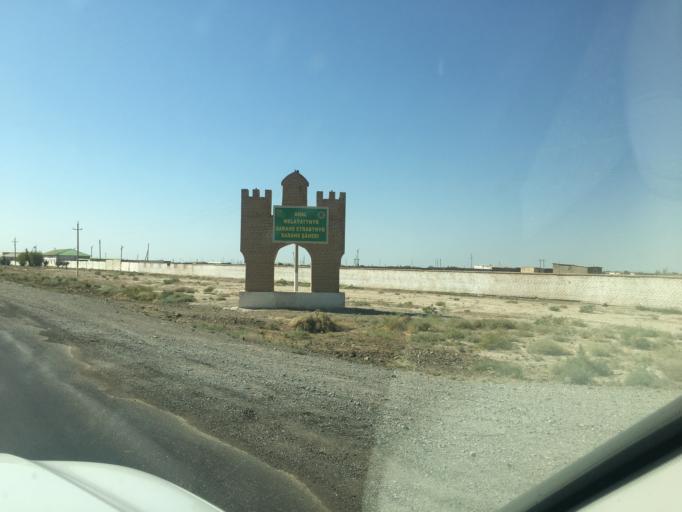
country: IR
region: Razavi Khorasan
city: Sarakhs
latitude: 36.5718
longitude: 61.2119
